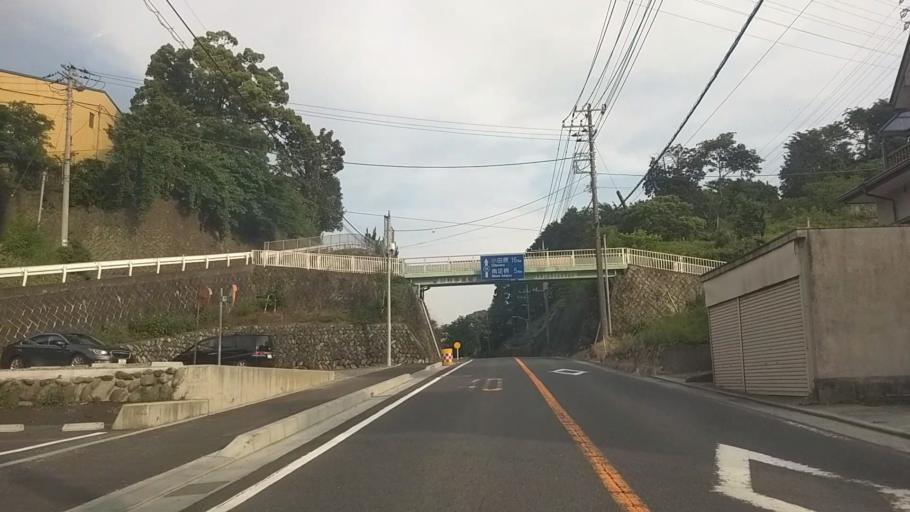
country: JP
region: Kanagawa
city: Odawara
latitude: 35.3582
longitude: 139.0885
